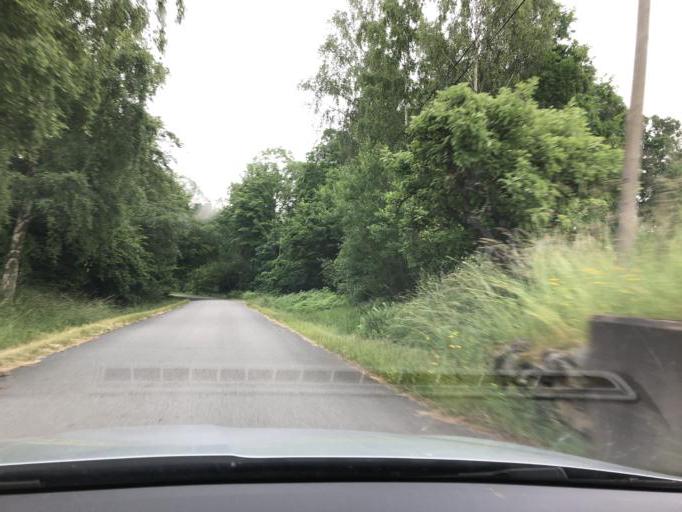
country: SE
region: Blekinge
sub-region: Solvesborgs Kommun
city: Soelvesborg
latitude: 56.1426
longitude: 14.6027
